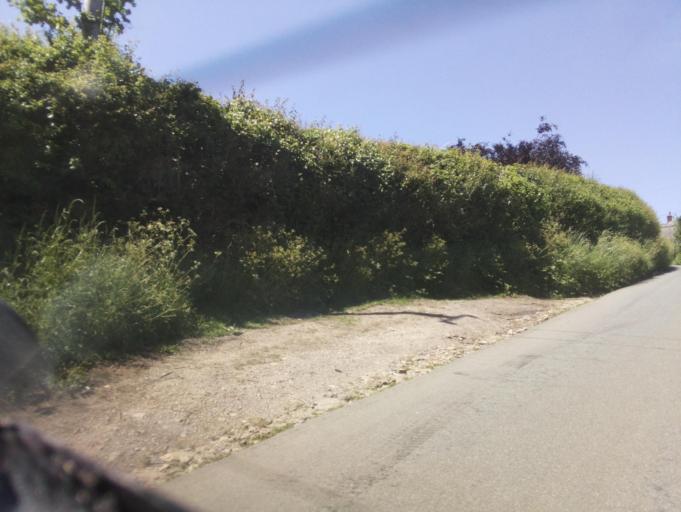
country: GB
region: England
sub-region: Wiltshire
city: Bremhill
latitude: 51.4486
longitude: -2.0292
